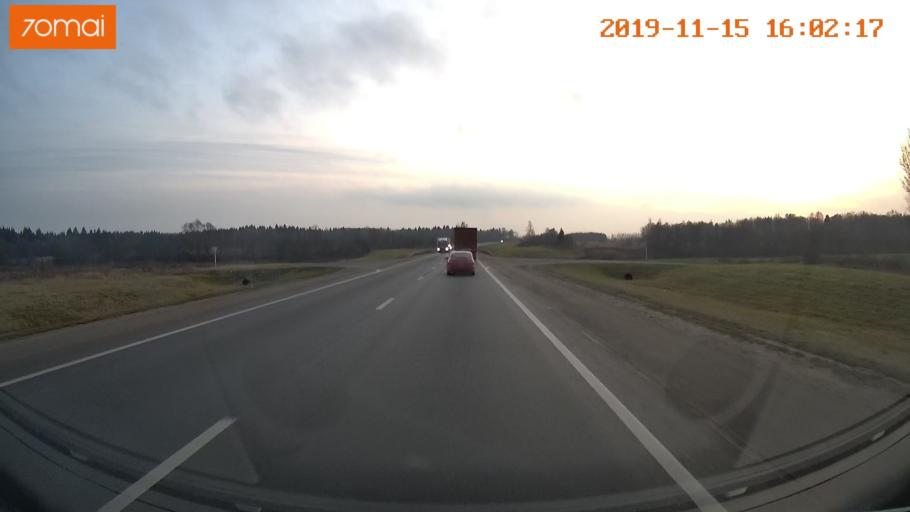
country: RU
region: Jaroslavl
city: Yaroslavl
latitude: 57.7731
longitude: 39.9256
